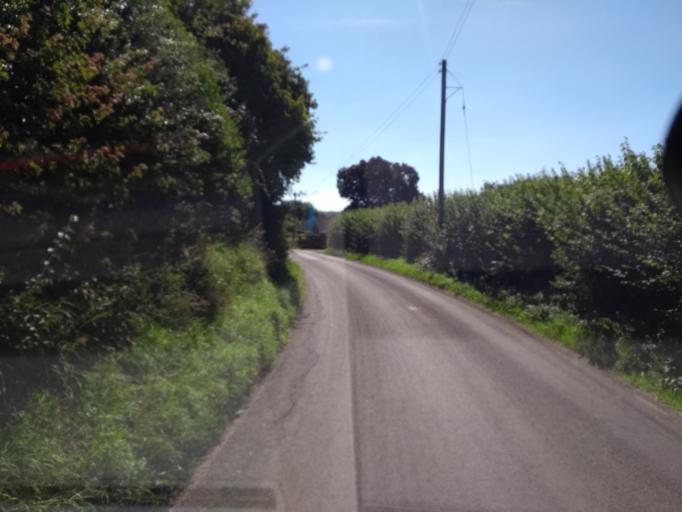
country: GB
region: England
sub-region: Somerset
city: Ilchester
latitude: 51.0563
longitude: -2.6961
